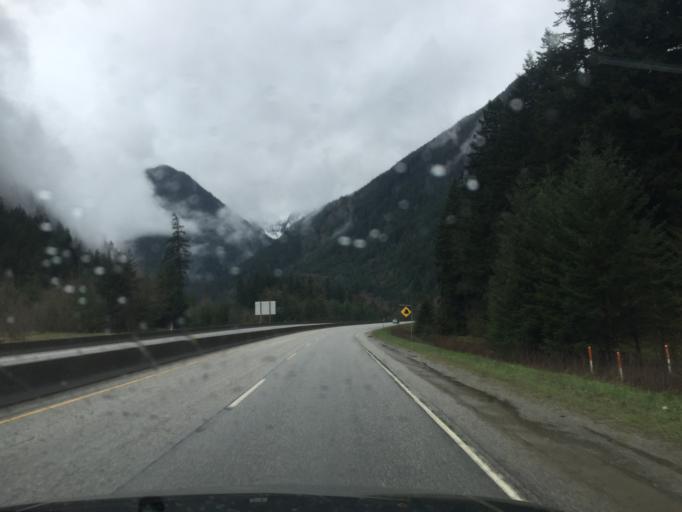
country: CA
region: British Columbia
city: Hope
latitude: 49.4402
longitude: -121.2899
